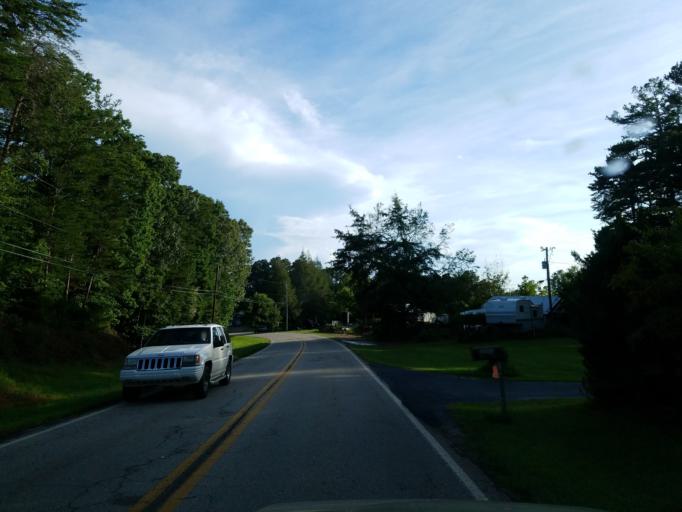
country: US
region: Georgia
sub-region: Lumpkin County
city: Dahlonega
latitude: 34.5571
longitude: -83.8857
